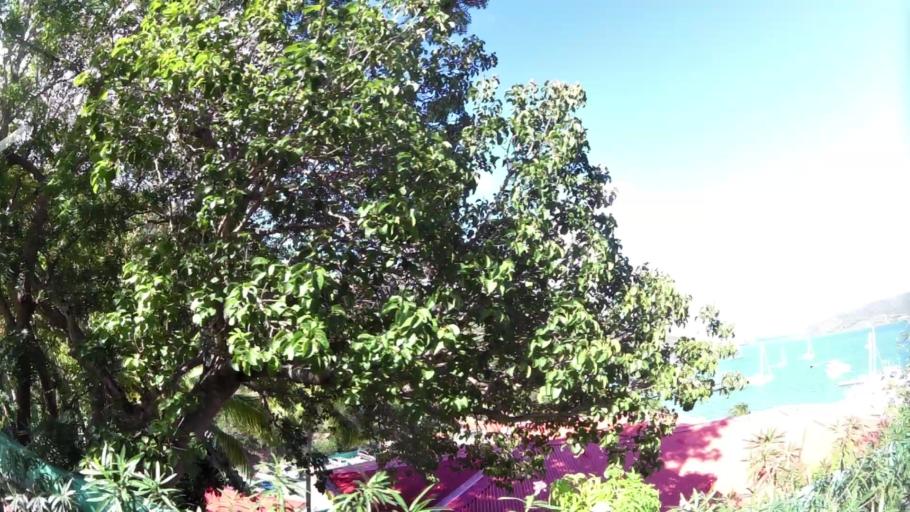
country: VG
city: Tortola
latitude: 18.4971
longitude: -64.3853
